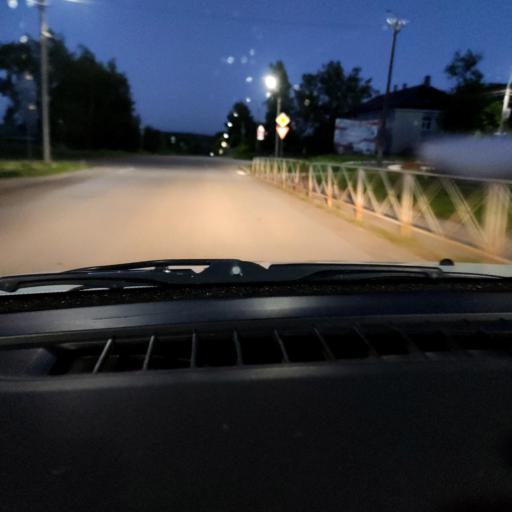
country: RU
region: Perm
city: Zvezdnyy
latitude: 57.7349
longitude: 56.3221
